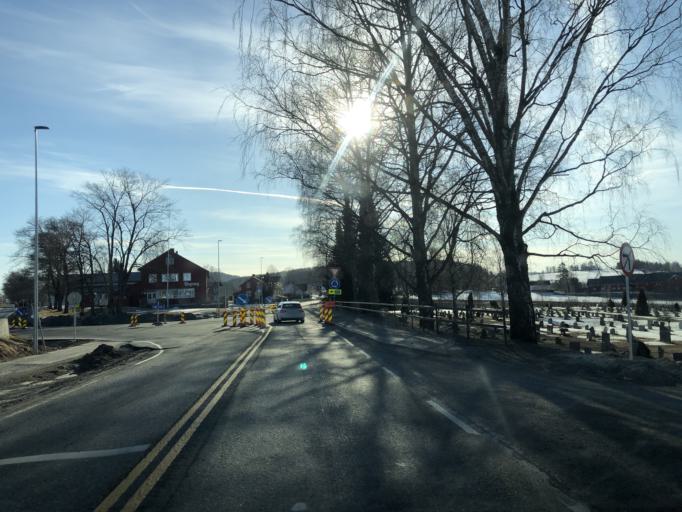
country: NO
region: Hedmark
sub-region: Ringsaker
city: Moelv
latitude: 60.9028
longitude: 10.7267
